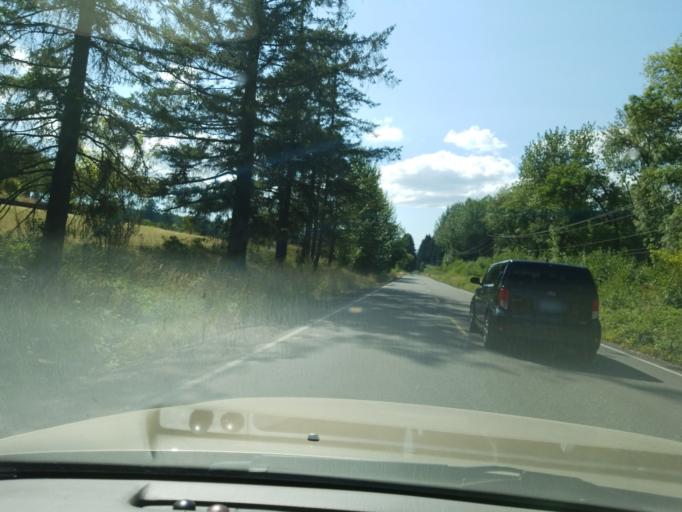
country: US
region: Oregon
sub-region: Yamhill County
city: Lafayette
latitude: 45.2989
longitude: -123.1186
